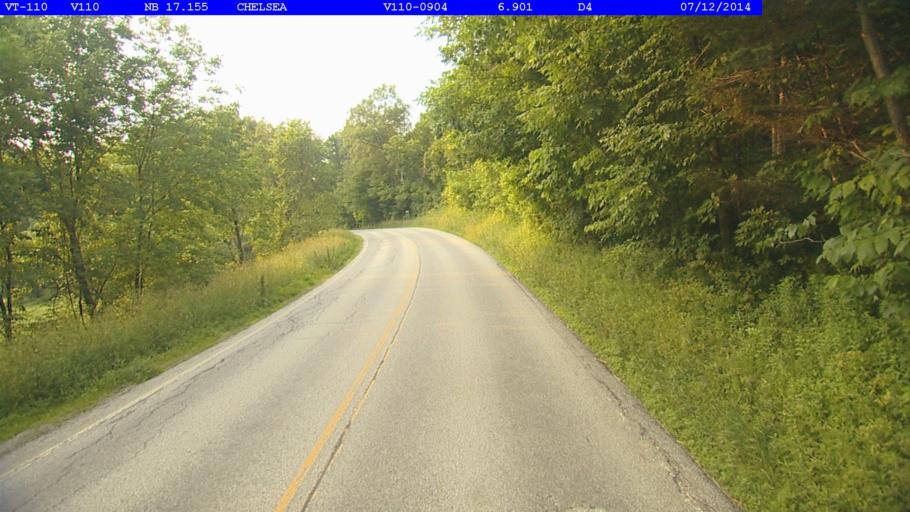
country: US
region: Vermont
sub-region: Orange County
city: Chelsea
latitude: 44.0399
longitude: -72.4740
